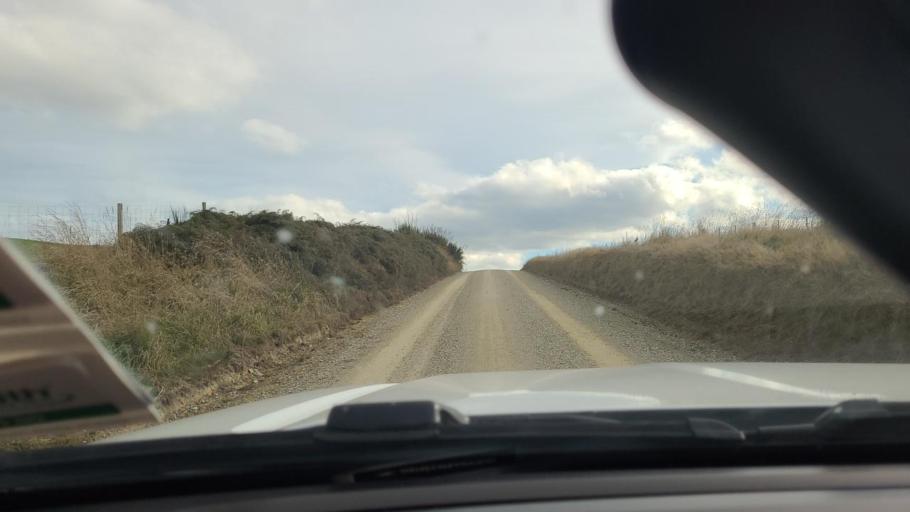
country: NZ
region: Southland
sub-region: Gore District
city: Gore
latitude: -45.7268
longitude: 168.7998
